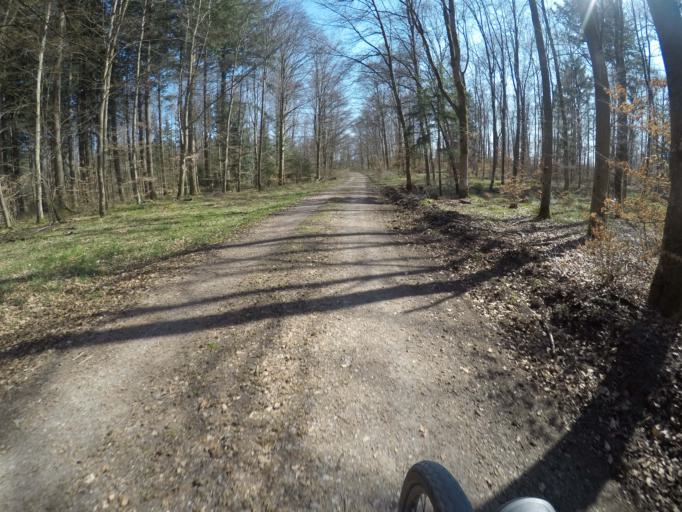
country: DE
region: Baden-Wuerttemberg
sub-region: Regierungsbezirk Stuttgart
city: Deckenpfronn
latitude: 48.6756
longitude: 8.8039
